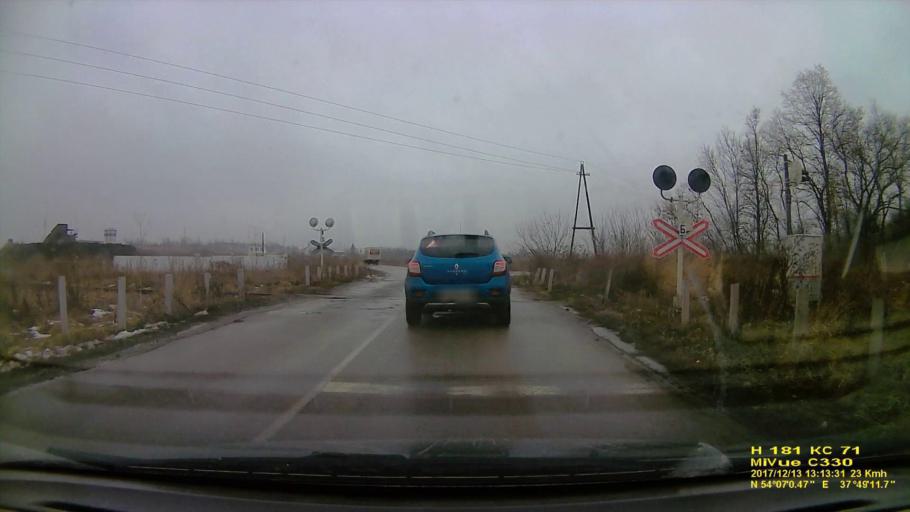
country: RU
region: Tula
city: Bolokhovo
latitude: 54.1168
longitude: 37.8197
